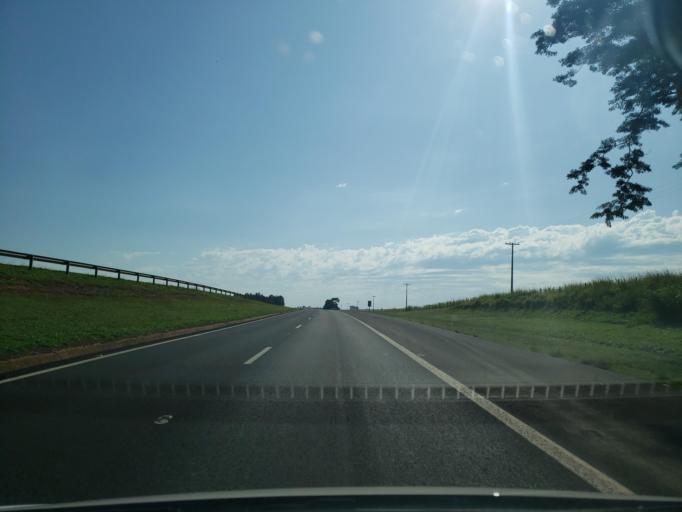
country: BR
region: Sao Paulo
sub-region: Penapolis
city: Penapolis
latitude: -21.5241
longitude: -49.9945
